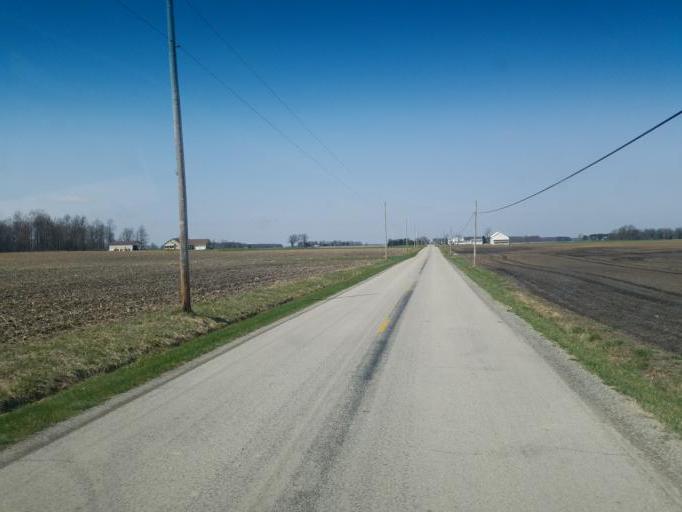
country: US
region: Ohio
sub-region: Wyandot County
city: Upper Sandusky
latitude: 40.8764
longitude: -83.2579
